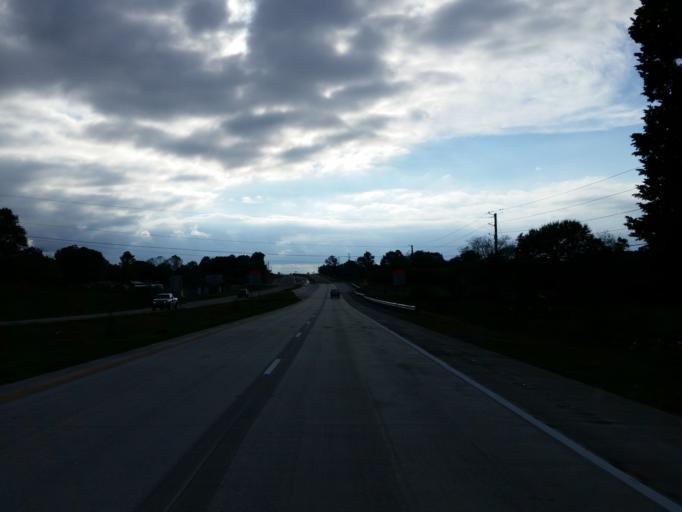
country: US
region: Georgia
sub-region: Bartow County
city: Euharlee
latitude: 34.1063
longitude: -84.9129
